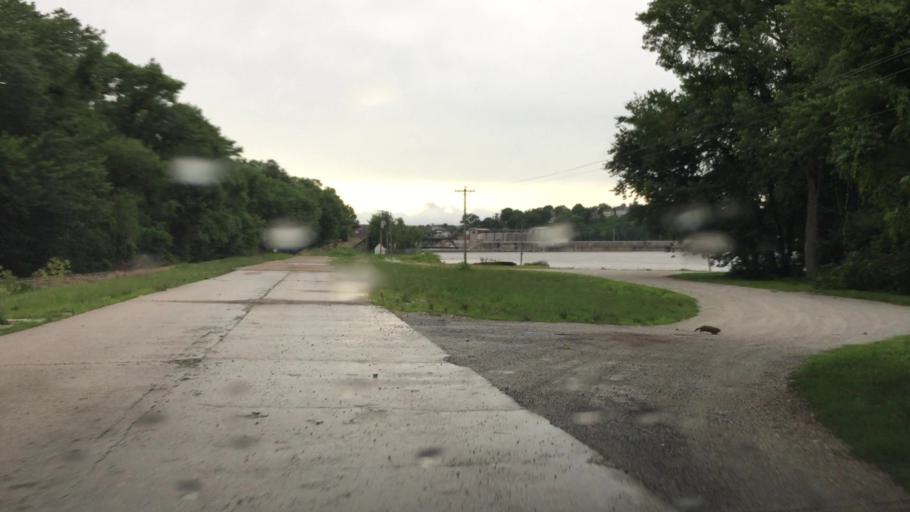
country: US
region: Iowa
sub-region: Lee County
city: Keokuk
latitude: 40.3893
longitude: -91.3647
